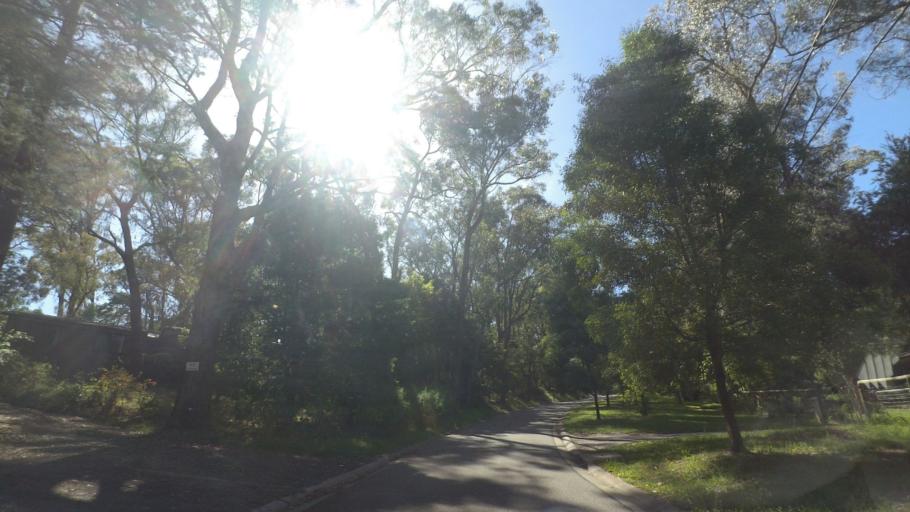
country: AU
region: Victoria
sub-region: Yarra Ranges
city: Kalorama
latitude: -37.8019
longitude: 145.3742
